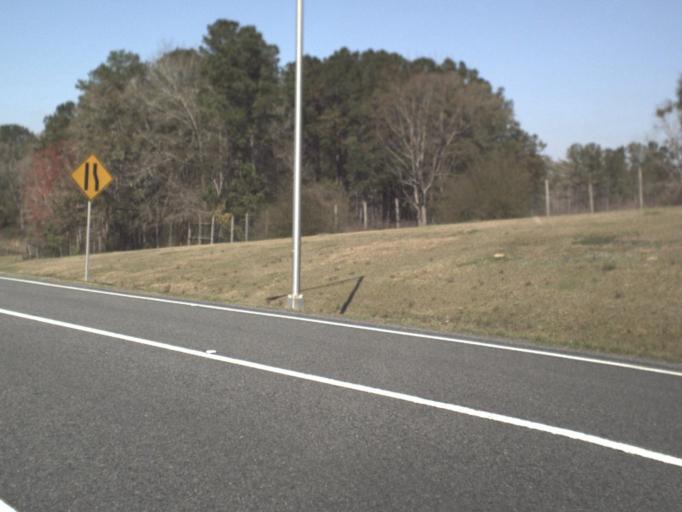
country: US
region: Florida
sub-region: Jackson County
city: Sneads
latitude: 30.6393
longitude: -84.9876
